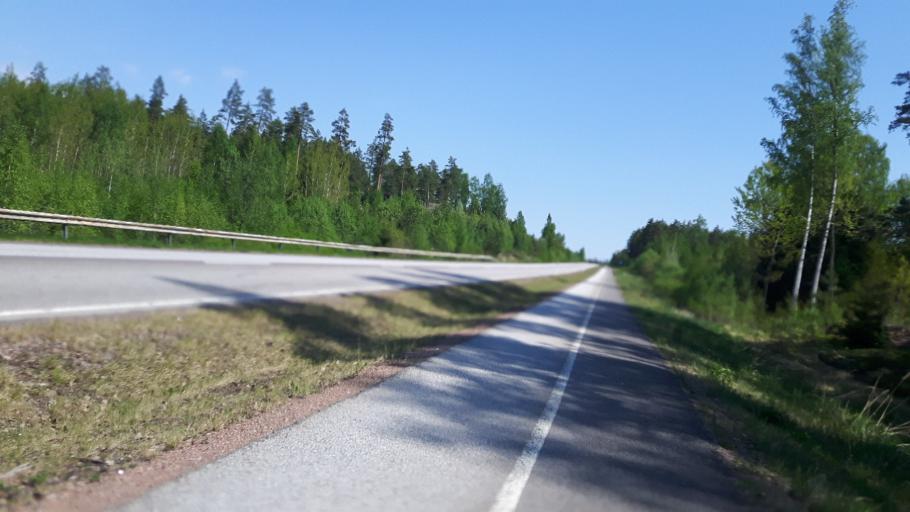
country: FI
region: Uusimaa
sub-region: Loviisa
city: Ruotsinpyhtaeae
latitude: 60.4847
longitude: 26.3994
